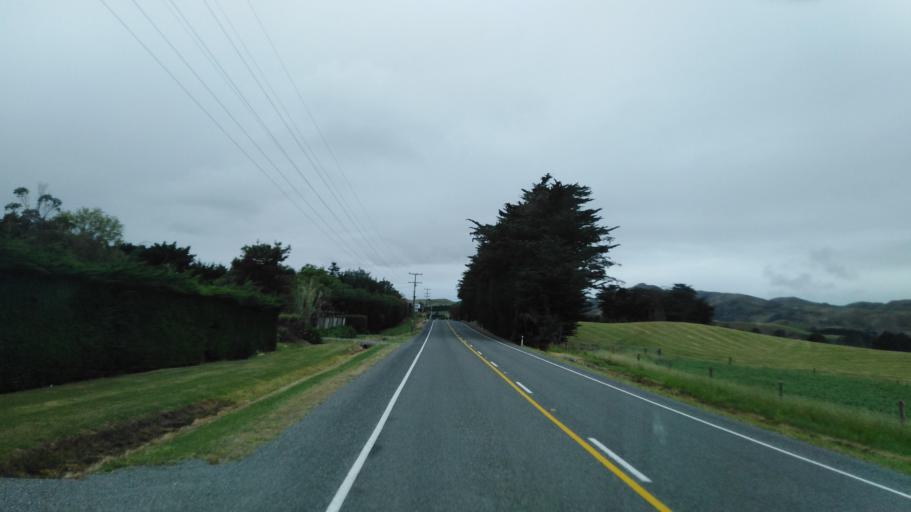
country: NZ
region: Marlborough
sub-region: Marlborough District
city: Blenheim
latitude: -41.8321
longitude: 174.1288
